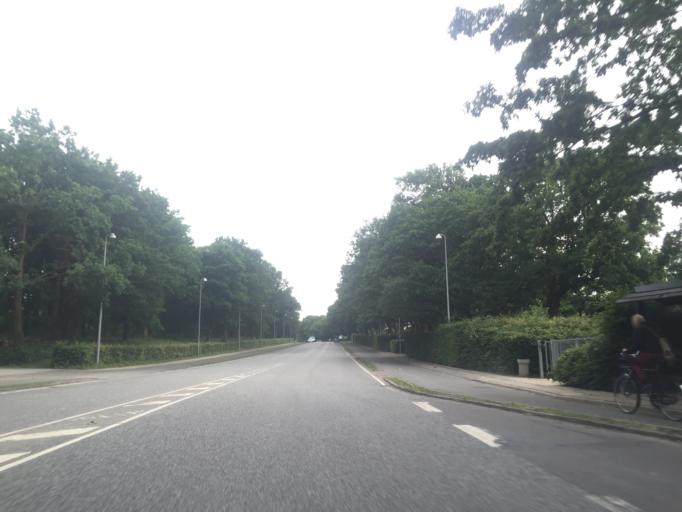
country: DK
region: Capital Region
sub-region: Lyngby-Tarbaek Kommune
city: Kongens Lyngby
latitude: 55.7856
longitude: 12.5140
